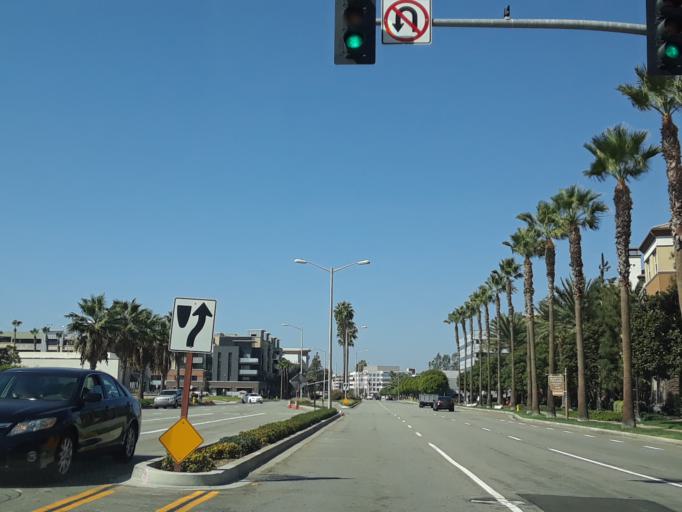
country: US
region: California
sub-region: Orange County
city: Irvine
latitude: 33.6817
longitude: -117.8416
